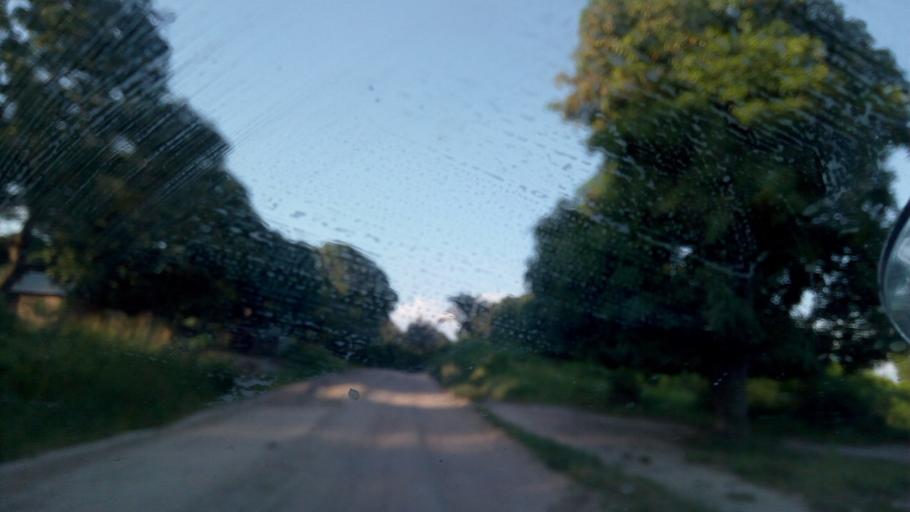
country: BI
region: Bururi
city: Rumonge
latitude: -4.1495
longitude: 29.0721
